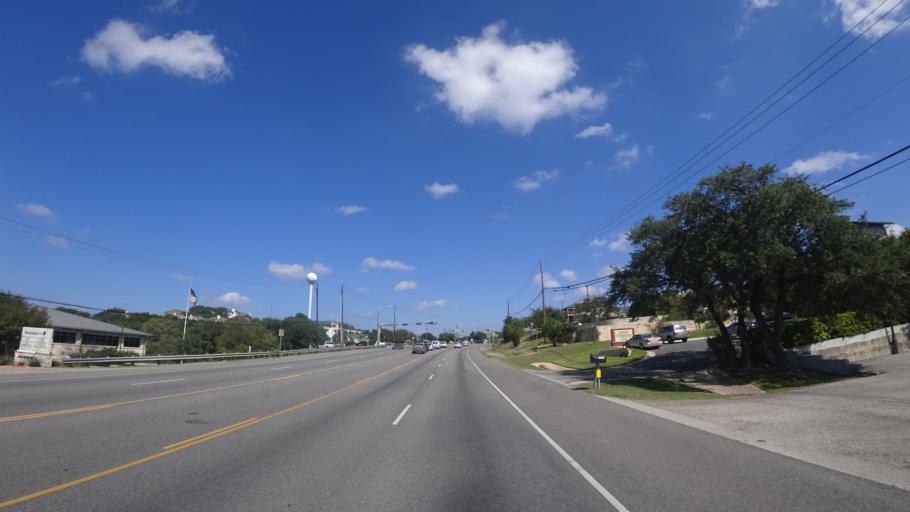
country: US
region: Texas
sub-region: Travis County
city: Lakeway
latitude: 30.3530
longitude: -97.9622
